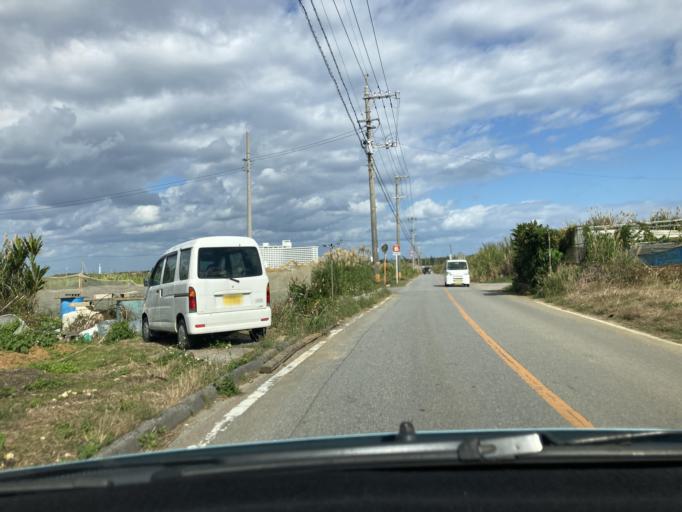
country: JP
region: Okinawa
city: Ishikawa
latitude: 26.4262
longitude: 127.7174
